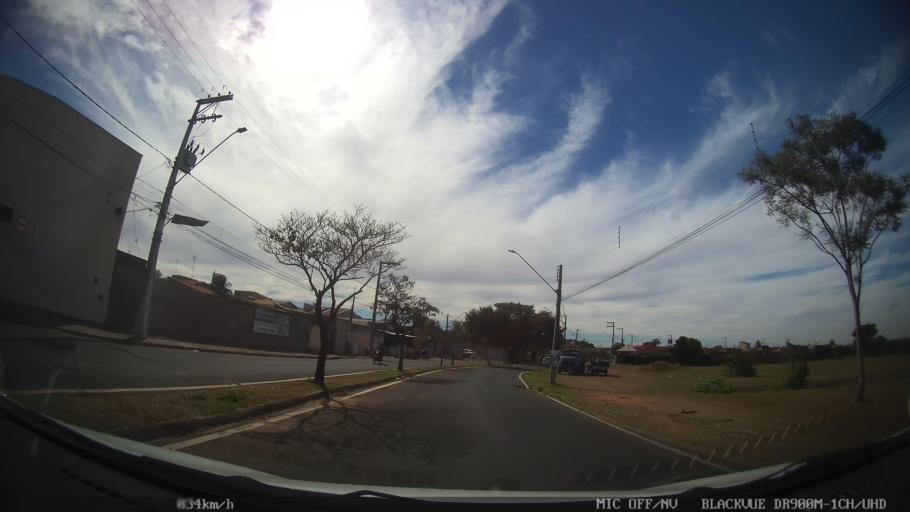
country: BR
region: Sao Paulo
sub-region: Catanduva
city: Catanduva
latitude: -21.1219
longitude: -48.9443
